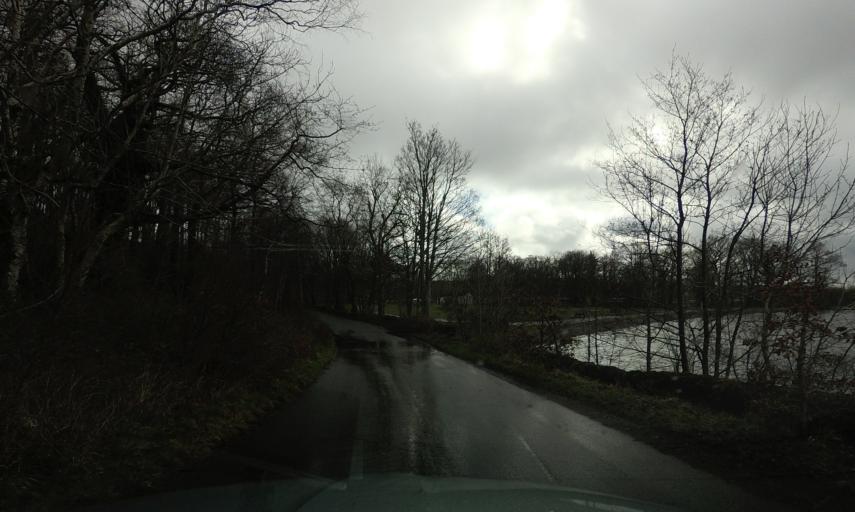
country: GB
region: Scotland
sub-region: West Dunbartonshire
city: Balloch
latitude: 56.1138
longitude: -4.5844
